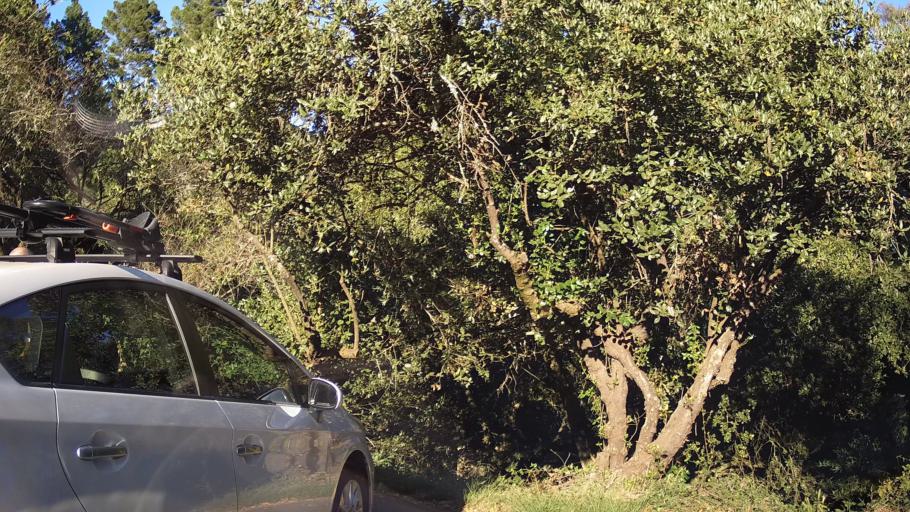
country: US
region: California
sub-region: Contra Costa County
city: Orinda
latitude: 37.8476
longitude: -122.1986
